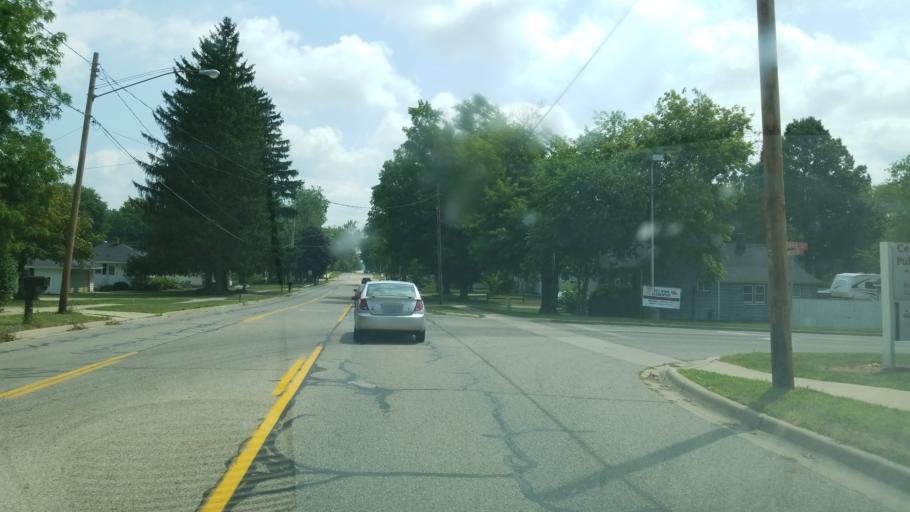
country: US
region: Michigan
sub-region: Kent County
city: Cedar Springs
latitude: 43.2200
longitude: -85.5464
